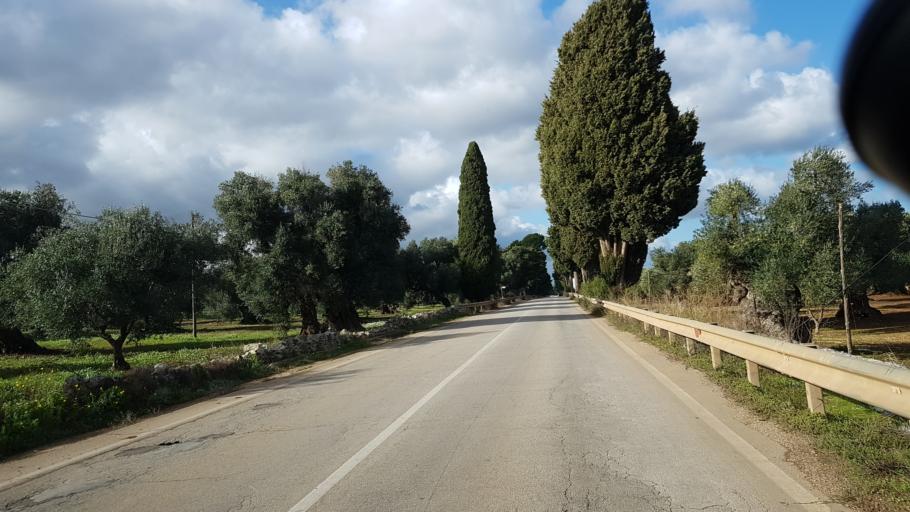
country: IT
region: Apulia
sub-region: Provincia di Brindisi
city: Ostuni
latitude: 40.7573
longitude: 17.5361
